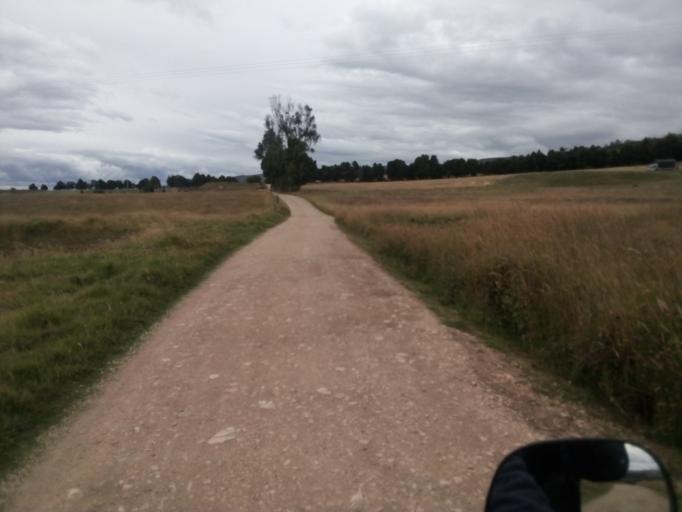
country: CO
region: Boyaca
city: Toca
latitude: 5.5903
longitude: -73.1366
